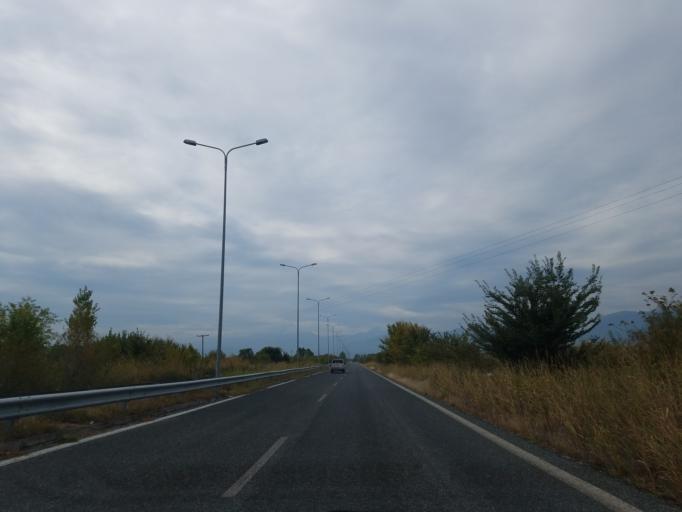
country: GR
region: Thessaly
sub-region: Trikala
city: Pyrgetos
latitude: 39.5645
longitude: 21.7377
